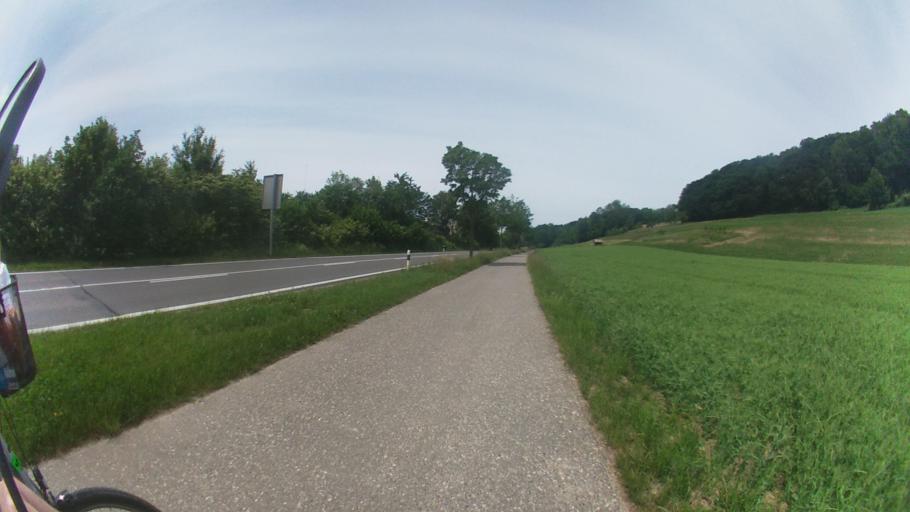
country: CH
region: Aargau
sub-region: Bezirk Zurzach
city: Oberendingen
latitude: 47.5291
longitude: 8.3173
